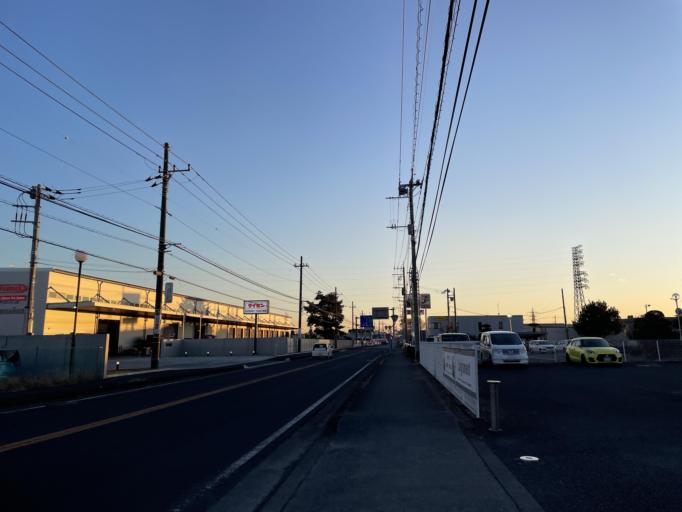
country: JP
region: Tochigi
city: Kaminokawa
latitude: 36.4535
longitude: 139.8670
